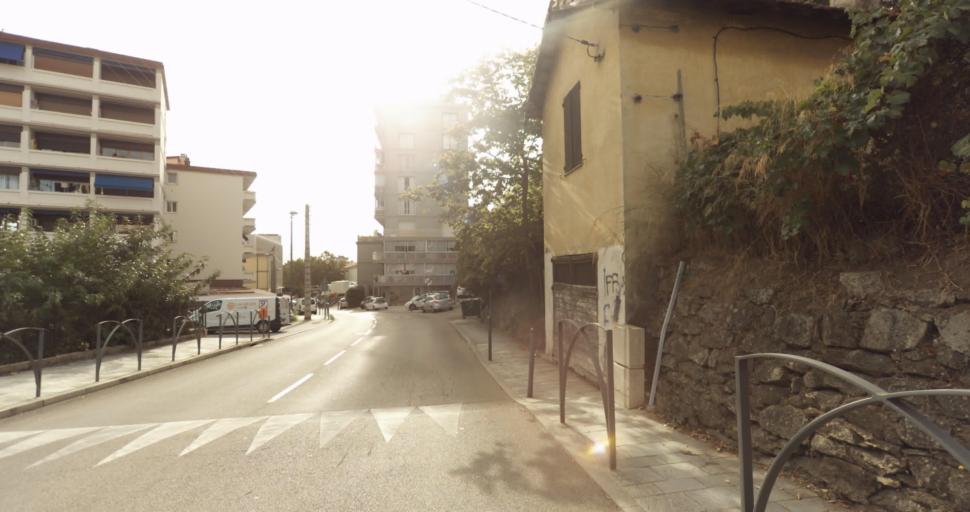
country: FR
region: Corsica
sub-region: Departement de la Corse-du-Sud
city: Ajaccio
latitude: 41.9288
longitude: 8.7330
